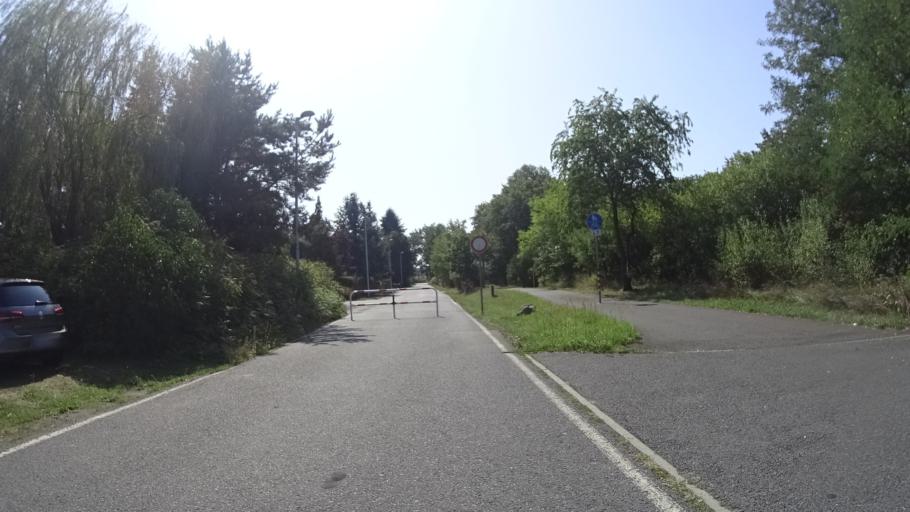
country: DE
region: Brandenburg
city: Cottbus
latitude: 51.7736
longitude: 14.3103
